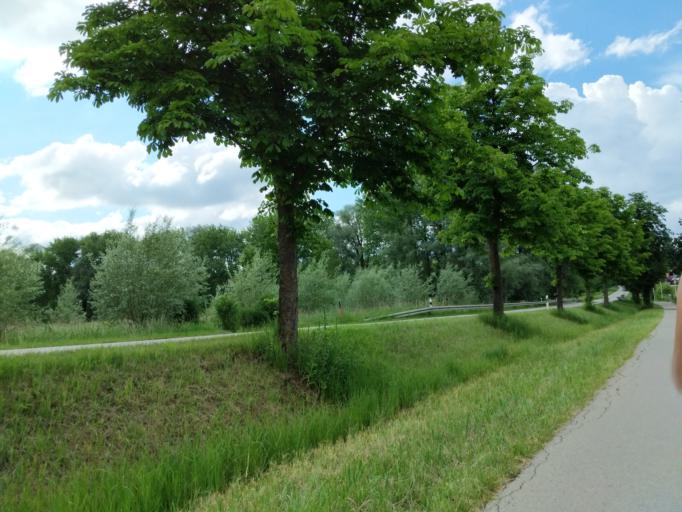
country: DE
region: Bavaria
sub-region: Upper Bavaria
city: Seefeld
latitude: 48.0360
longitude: 11.2007
